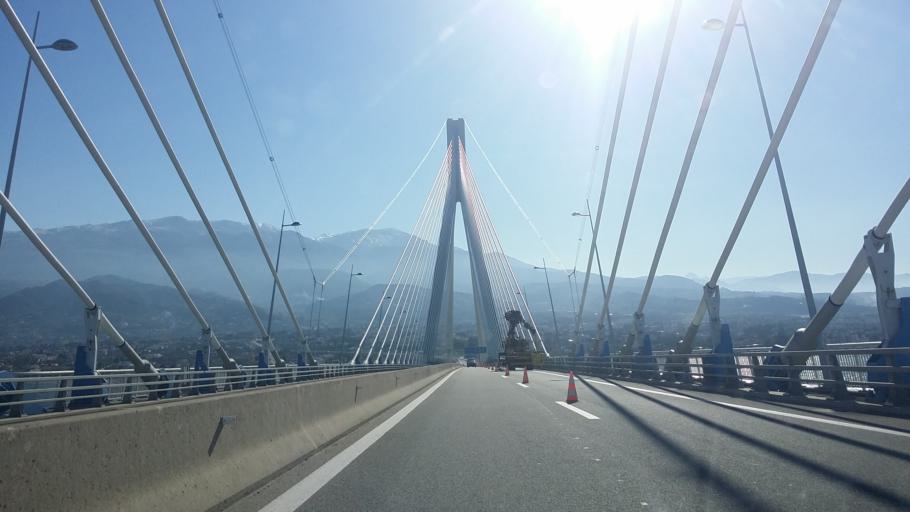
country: GR
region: West Greece
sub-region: Nomos Aitolias kai Akarnanias
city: Antirrio
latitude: 38.3164
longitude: 21.7751
